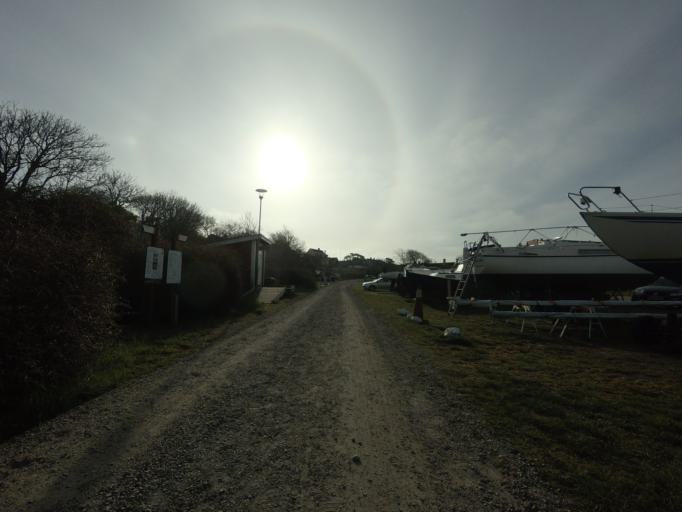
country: SE
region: Skane
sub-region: Hoganas Kommun
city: Hoganas
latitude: 56.2579
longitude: 12.5213
